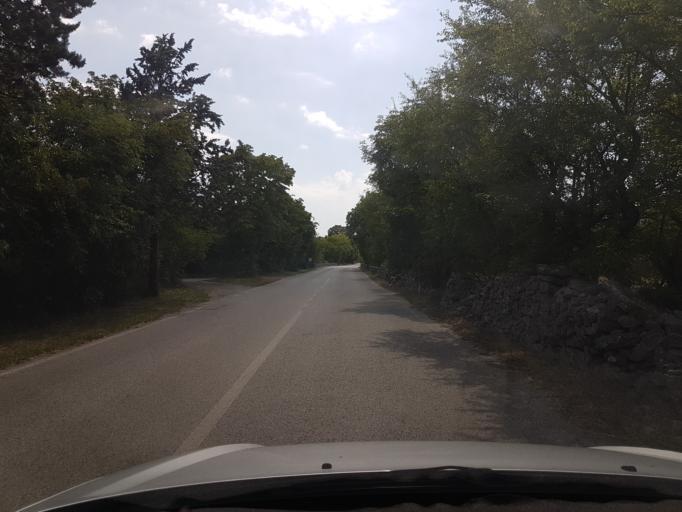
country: IT
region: Friuli Venezia Giulia
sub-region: Provincia di Trieste
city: Zolla
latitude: 45.7175
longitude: 13.7823
